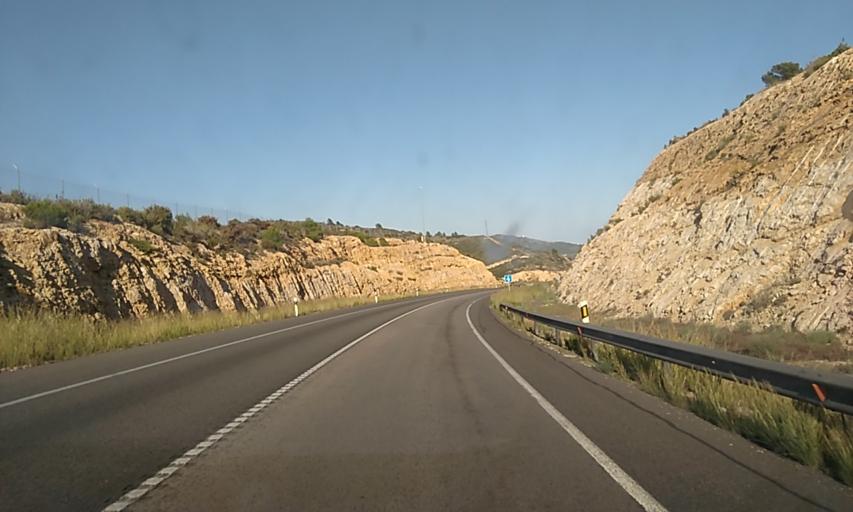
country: ES
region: Valencia
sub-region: Provincia de Castello
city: Torreblanca
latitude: 40.2257
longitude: 0.1786
